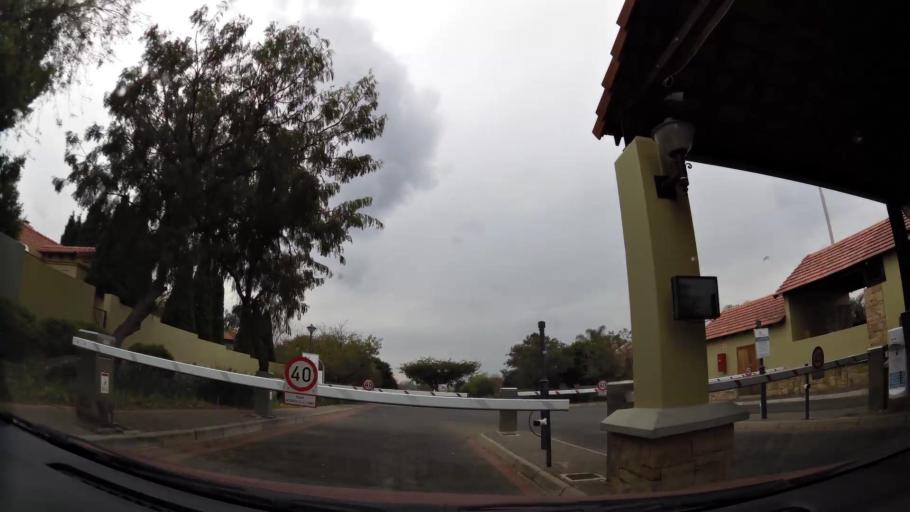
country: ZA
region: Gauteng
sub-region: City of Johannesburg Metropolitan Municipality
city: Roodepoort
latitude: -26.0972
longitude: 27.9189
